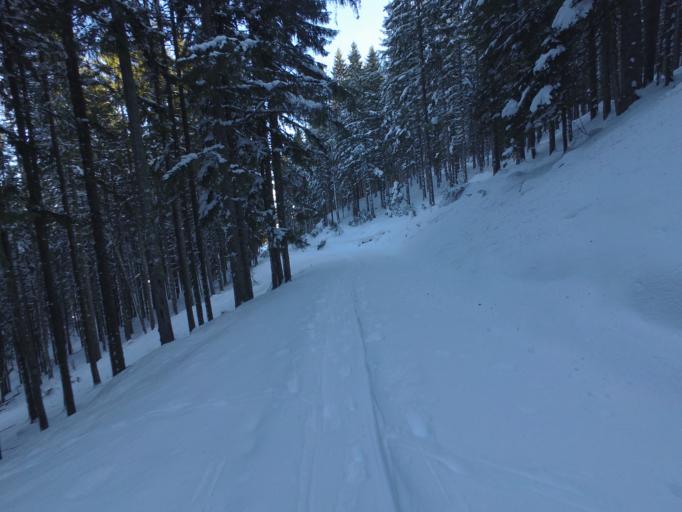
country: AT
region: Salzburg
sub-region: Politischer Bezirk Zell am See
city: Taxenbach
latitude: 47.2796
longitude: 13.0069
